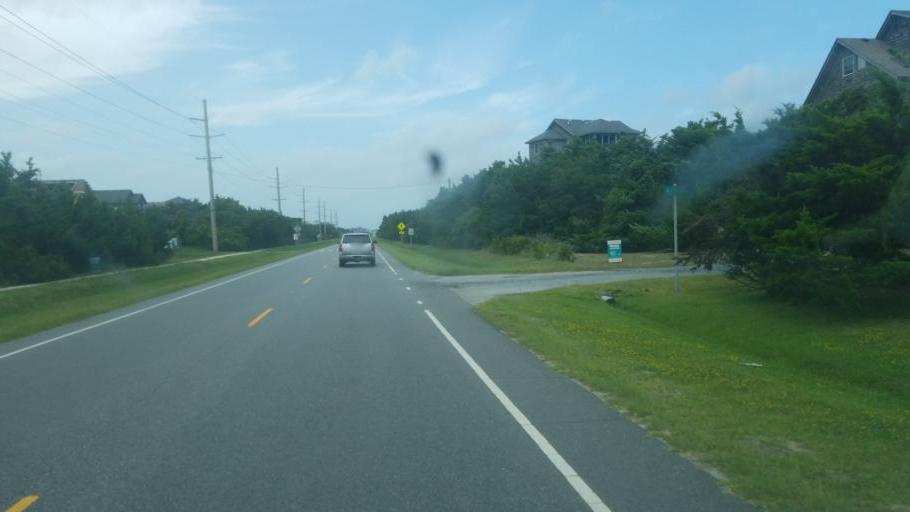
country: US
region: North Carolina
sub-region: Dare County
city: Buxton
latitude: 35.3258
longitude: -75.5083
